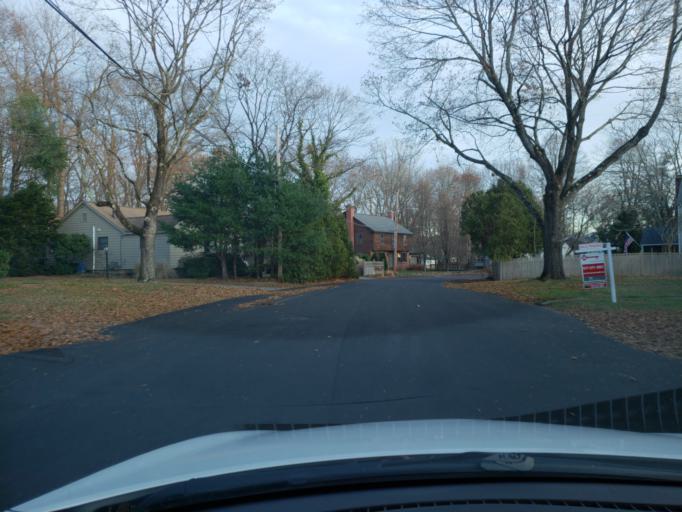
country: US
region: Massachusetts
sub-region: Essex County
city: Andover
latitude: 42.6610
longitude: -71.1355
